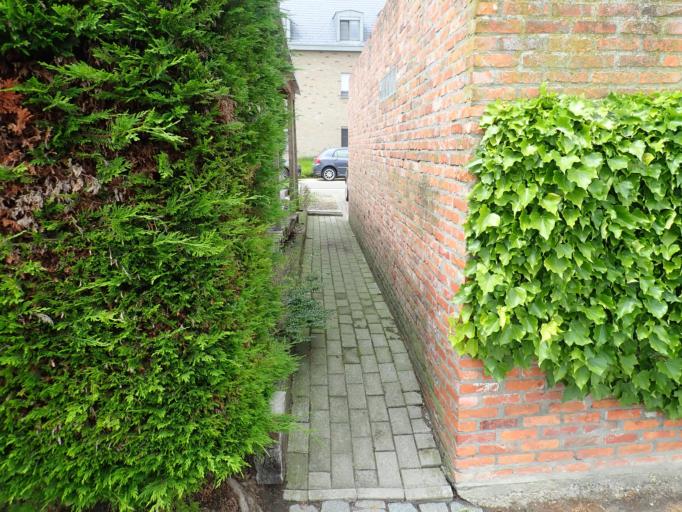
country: BE
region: Flanders
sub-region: Provincie Antwerpen
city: Heist-op-den-Berg
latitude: 51.1013
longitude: 4.7353
